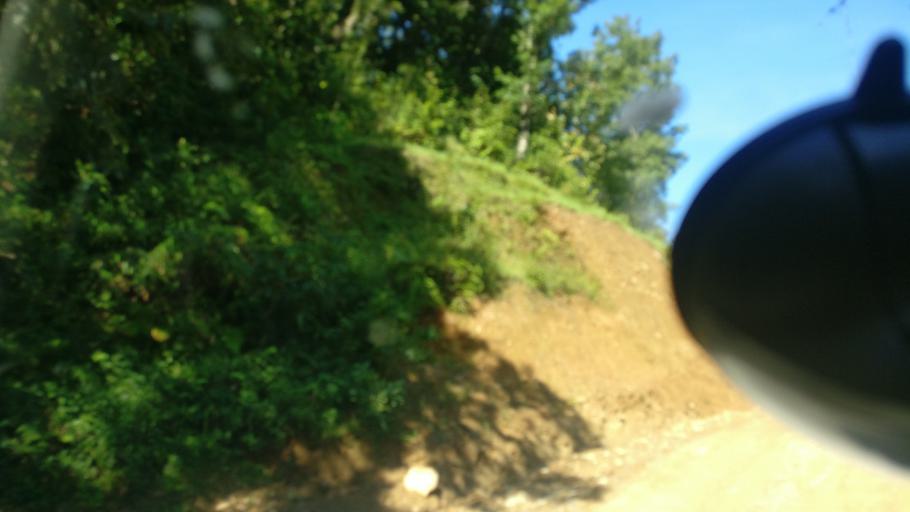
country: NP
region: Western Region
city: Baglung
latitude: 28.1452
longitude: 83.6523
